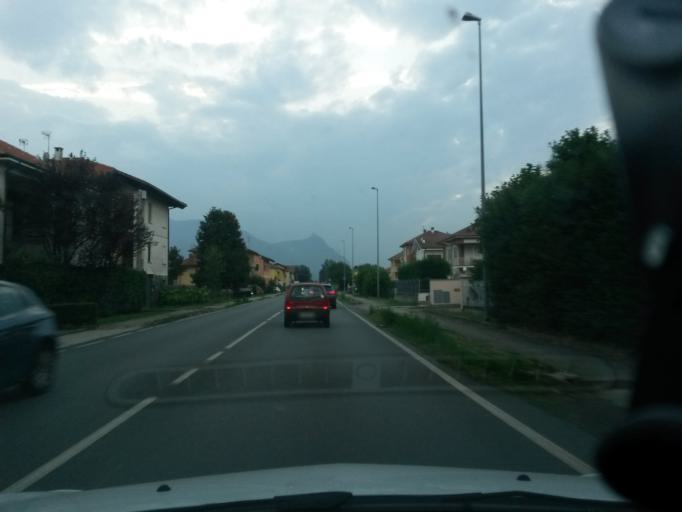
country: IT
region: Piedmont
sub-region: Provincia di Torino
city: Drubiaglio-Grangia
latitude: 45.0947
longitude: 7.4244
